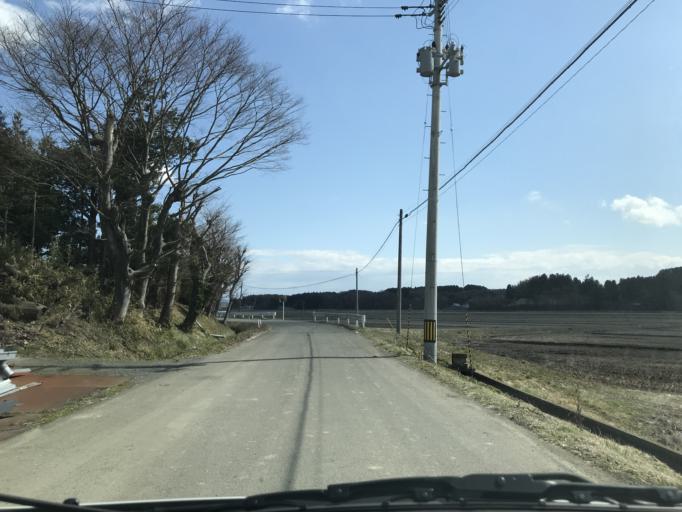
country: JP
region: Miyagi
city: Wakuya
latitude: 38.6793
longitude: 141.1310
